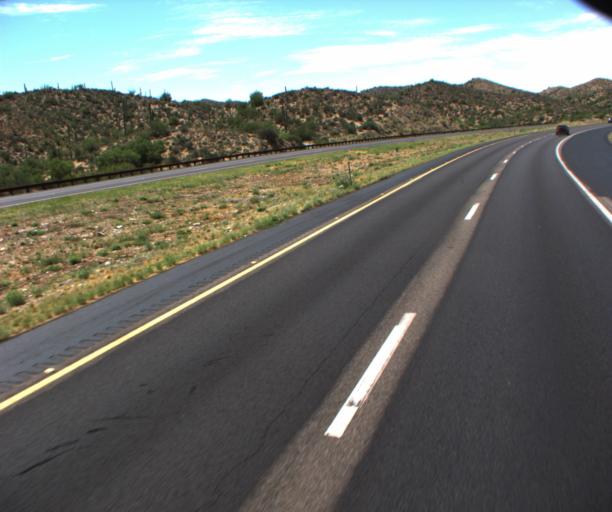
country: US
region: Arizona
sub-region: Pinal County
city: Gold Camp
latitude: 33.2730
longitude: -111.2142
